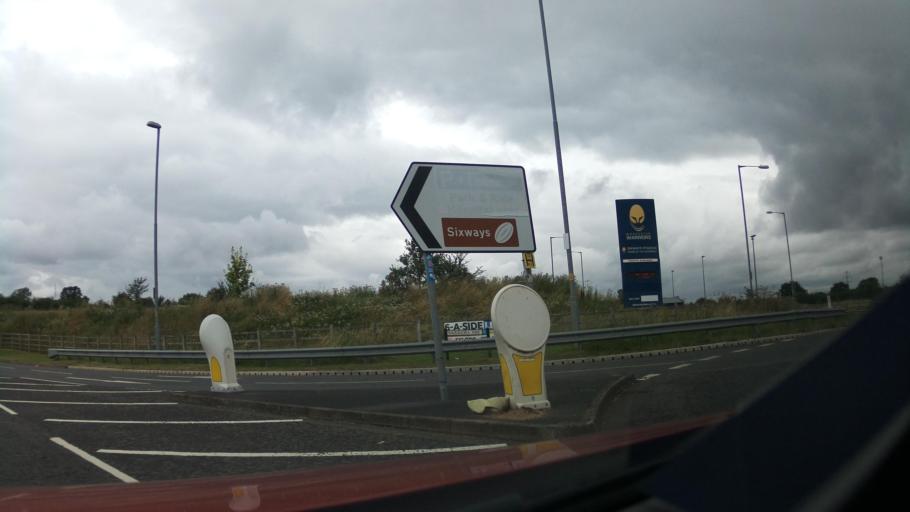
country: GB
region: England
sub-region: Worcestershire
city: Fernhill Heath
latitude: 52.2168
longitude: -2.1607
